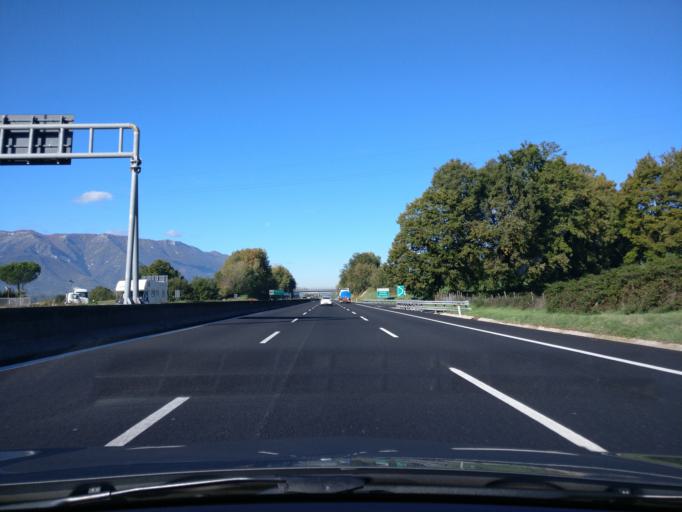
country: IT
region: Latium
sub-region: Provincia di Frosinone
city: Frosinone
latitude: 41.6246
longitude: 13.2983
